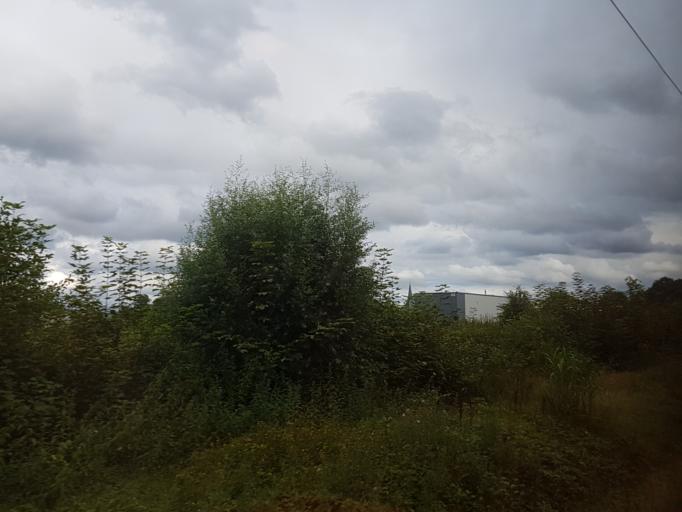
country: BE
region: Flanders
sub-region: Provincie Antwerpen
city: Kapellen
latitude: 51.2990
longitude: 4.4329
